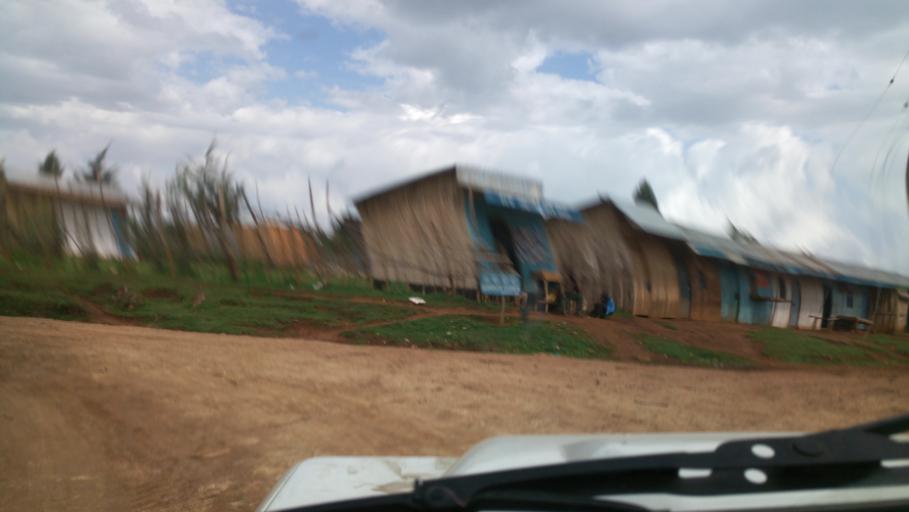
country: KE
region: Nakuru
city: Molo
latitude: -0.4305
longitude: 35.5858
